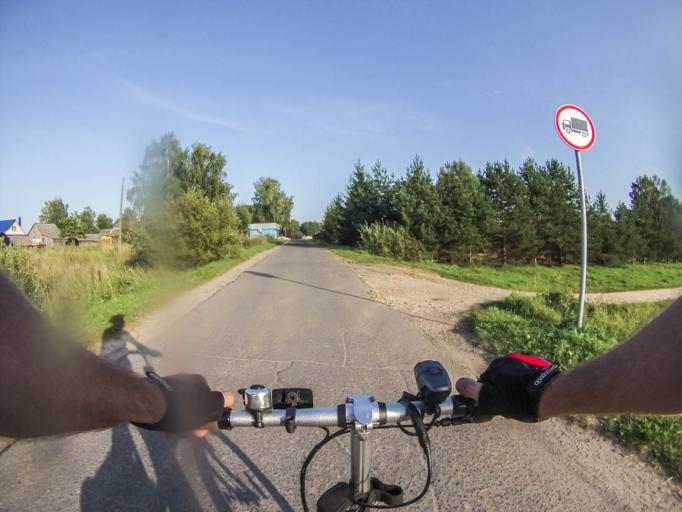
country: RU
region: Jaroslavl
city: Myshkin
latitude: 57.7483
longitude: 38.4349
